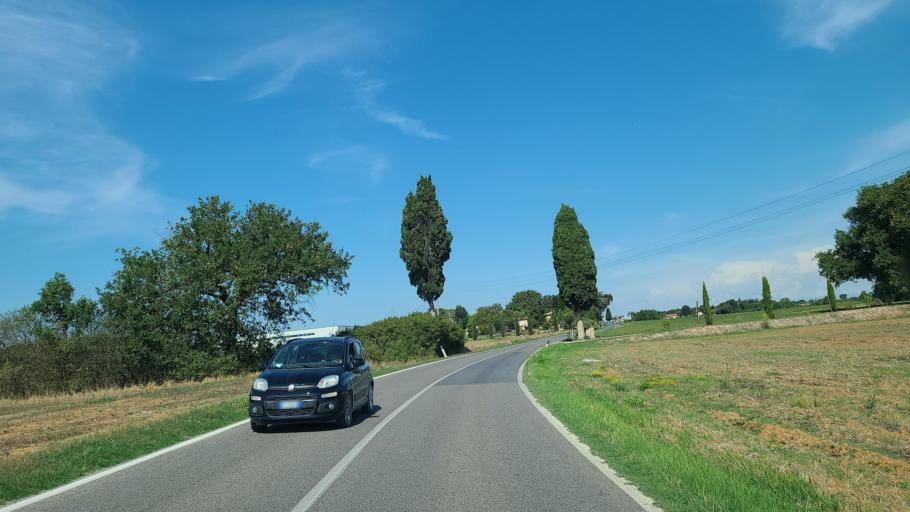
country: IT
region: Tuscany
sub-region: Provincia di Siena
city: Staggia
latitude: 43.4032
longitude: 11.1710
